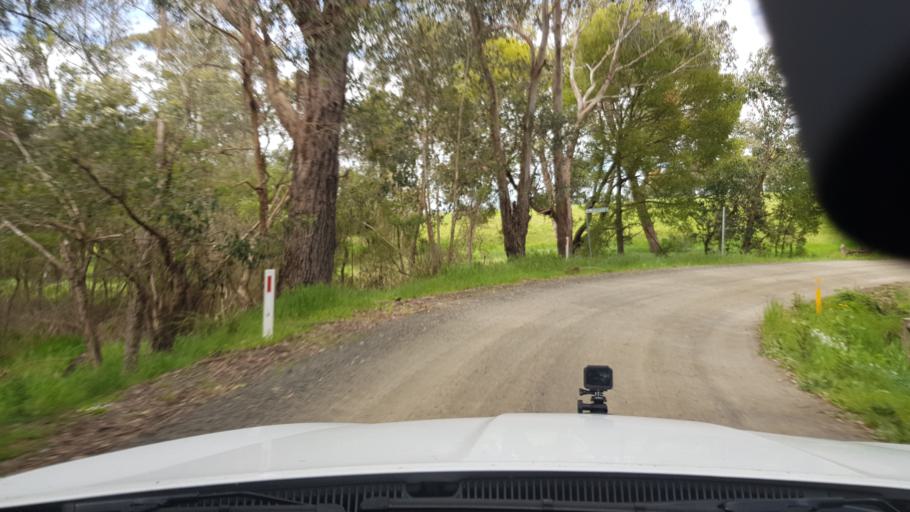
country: AU
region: Victoria
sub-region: Latrobe
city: Moe
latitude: -38.1631
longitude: 146.1351
